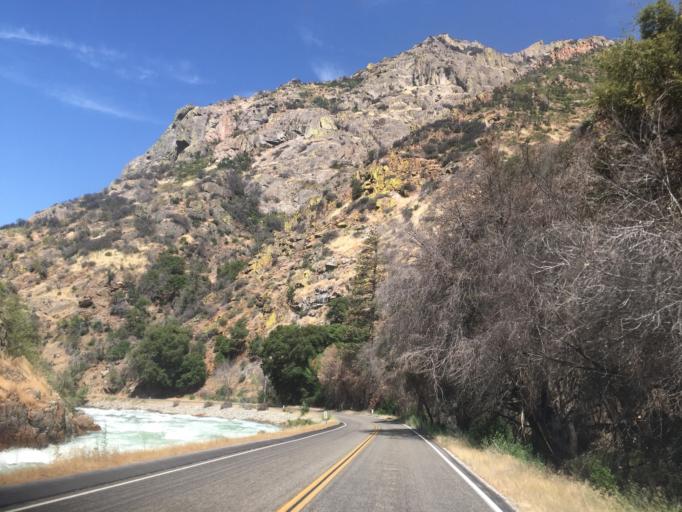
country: US
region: California
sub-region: Tulare County
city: Three Rivers
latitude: 36.8093
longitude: -118.7893
